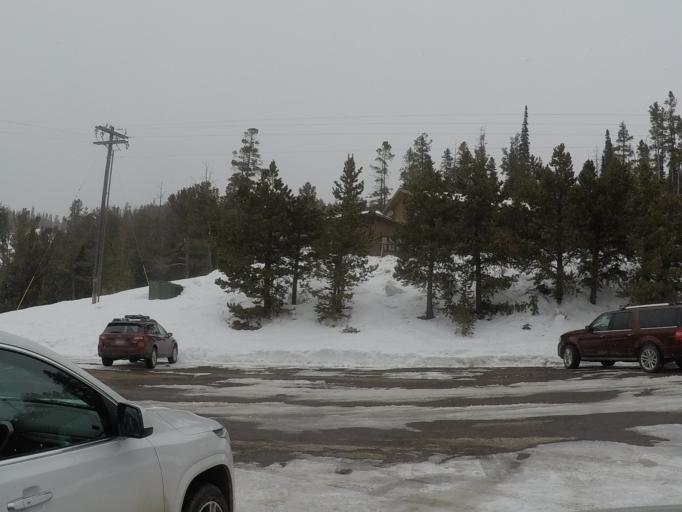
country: US
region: Montana
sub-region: Meagher County
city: White Sulphur Springs
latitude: 46.8318
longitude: -110.6792
